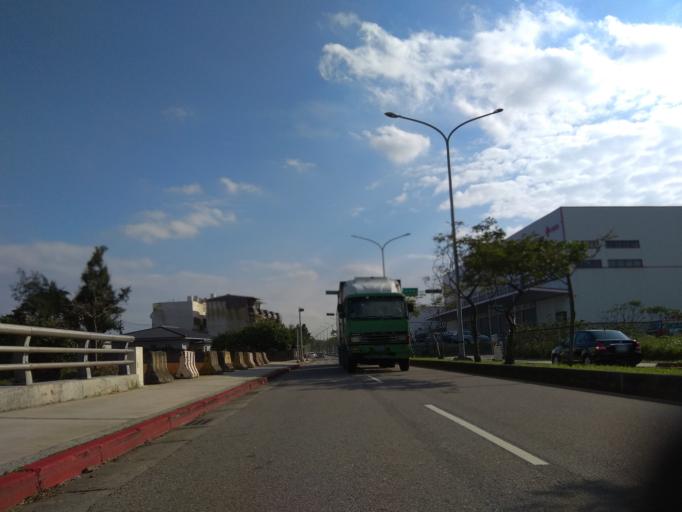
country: TW
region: Taiwan
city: Taoyuan City
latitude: 25.0620
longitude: 121.1779
